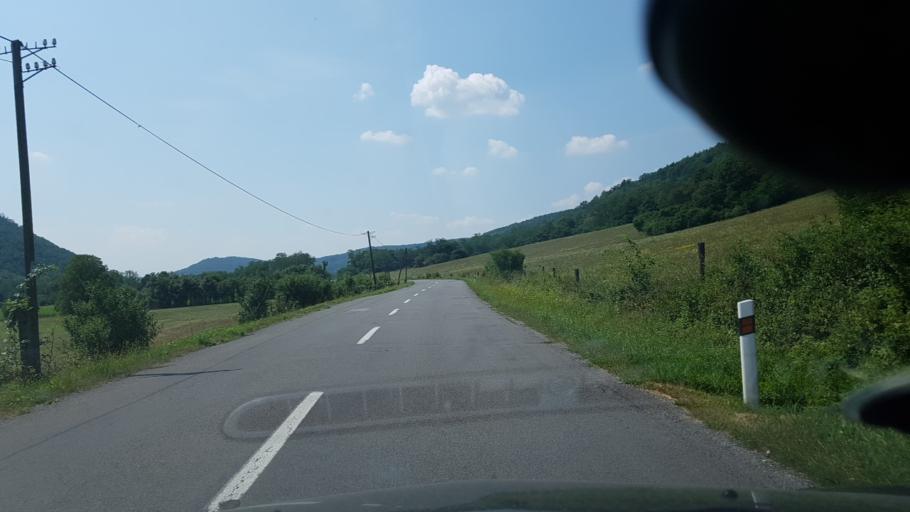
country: SK
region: Banskobystricky
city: Velky Krtis
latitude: 48.3206
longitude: 19.4064
